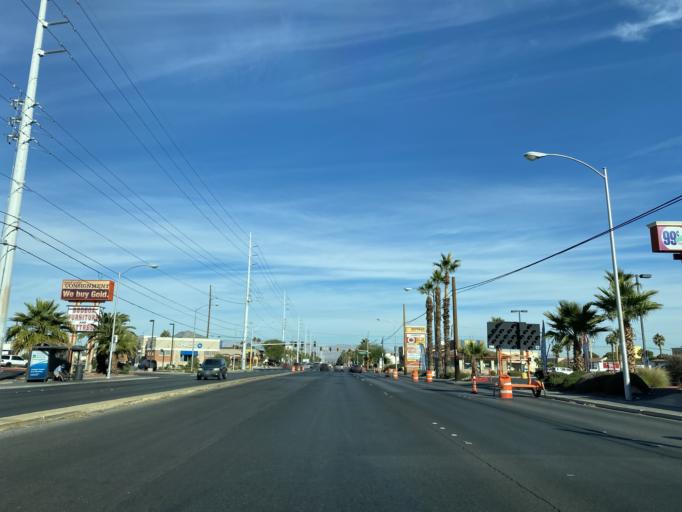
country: US
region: Nevada
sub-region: Clark County
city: Paradise
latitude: 36.0986
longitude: -115.1189
